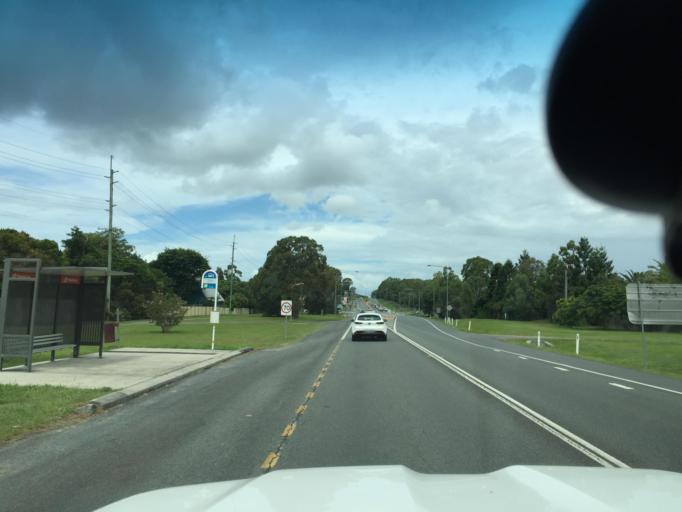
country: AU
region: Queensland
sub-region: Moreton Bay
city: Deception Bay
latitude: -27.1887
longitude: 153.0141
